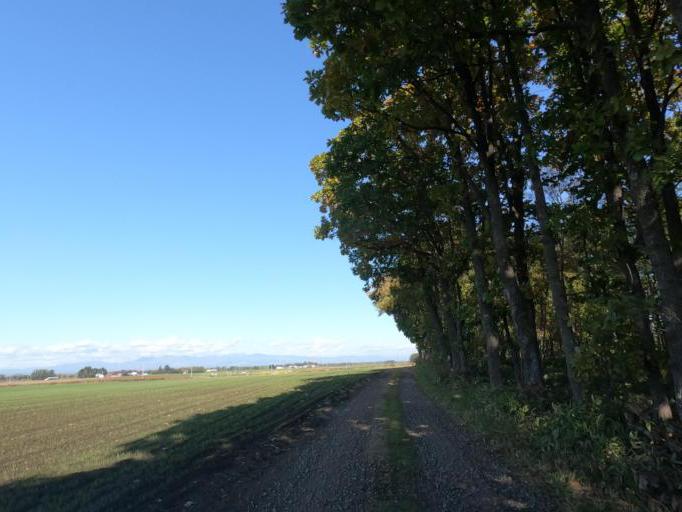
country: JP
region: Hokkaido
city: Otofuke
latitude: 43.0147
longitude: 143.2695
